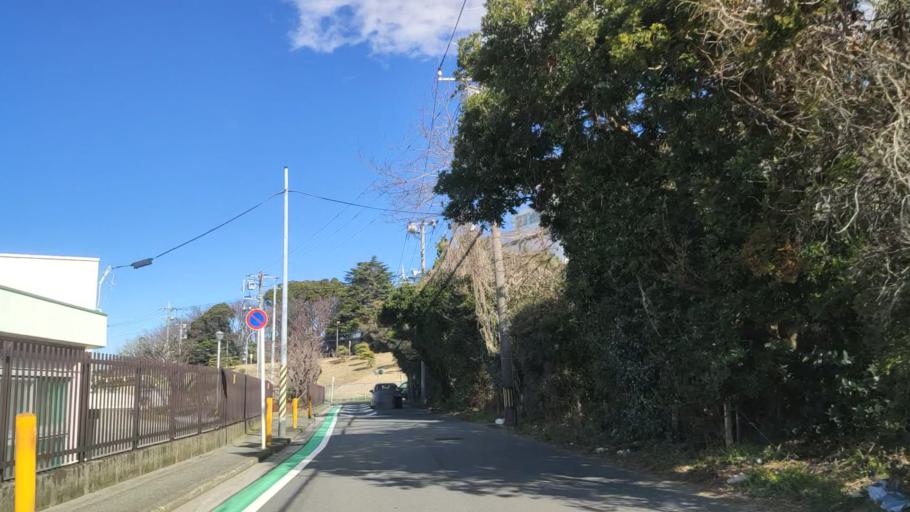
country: JP
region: Kanagawa
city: Yokohama
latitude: 35.4851
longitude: 139.5756
